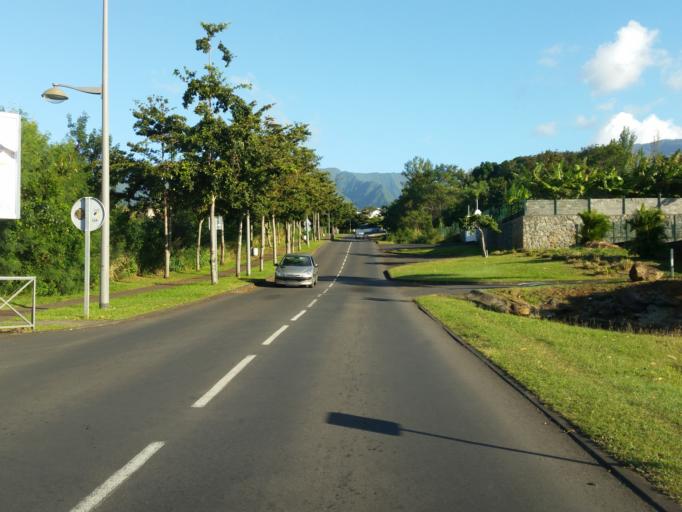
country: RE
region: Reunion
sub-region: Reunion
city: Sainte-Marie
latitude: -20.9039
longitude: 55.4983
